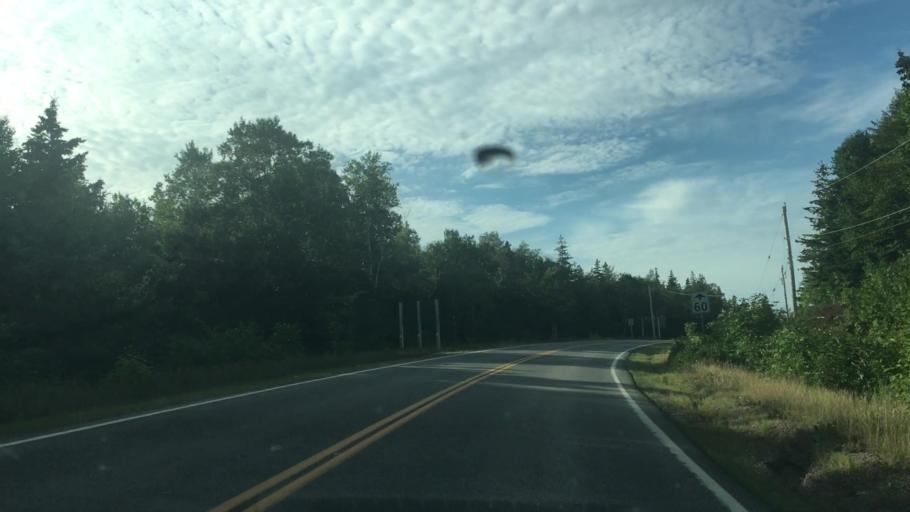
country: CA
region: Nova Scotia
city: Sydney Mines
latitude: 46.8181
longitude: -60.7947
